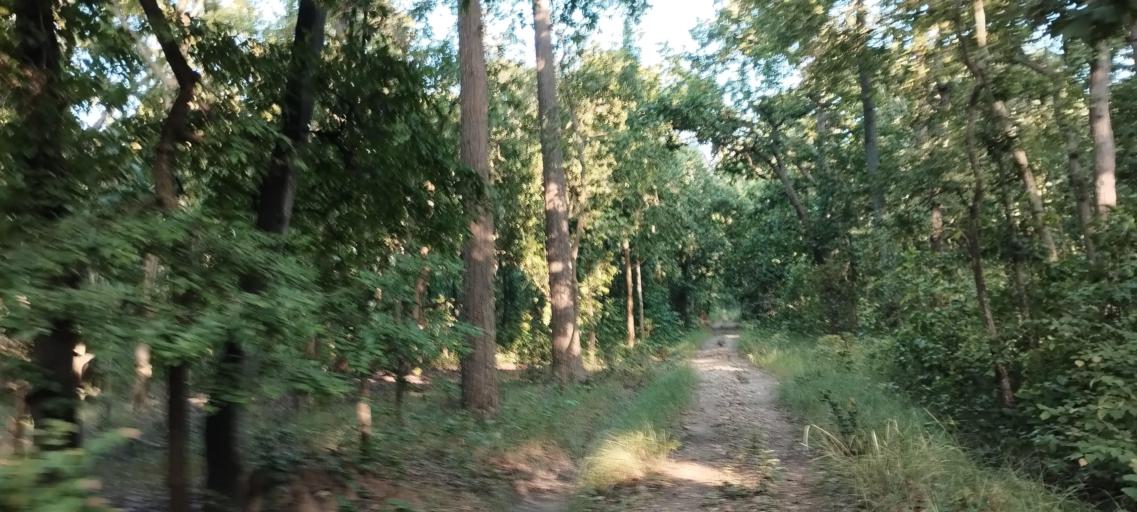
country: NP
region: Far Western
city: Tikapur
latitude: 28.4879
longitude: 81.2596
